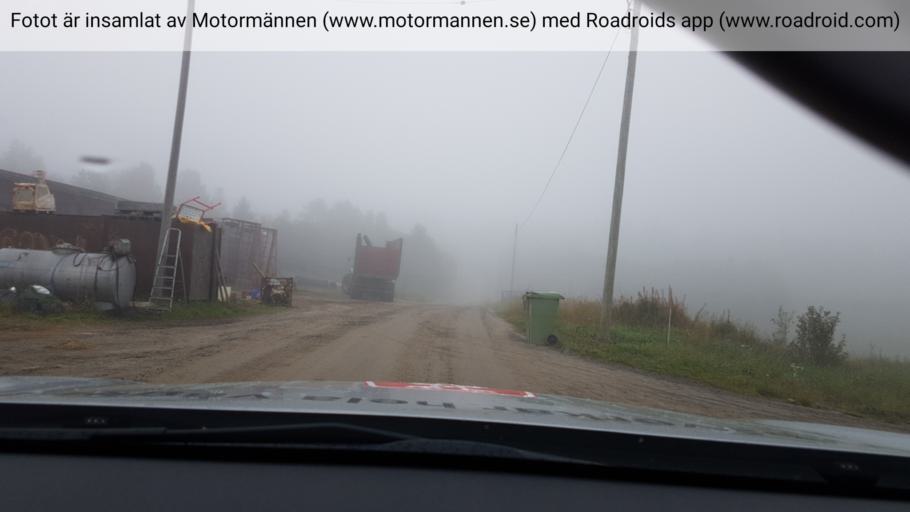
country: SE
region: Vaesterbotten
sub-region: Umea Kommun
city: Ersmark
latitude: 64.0876
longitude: 20.2177
